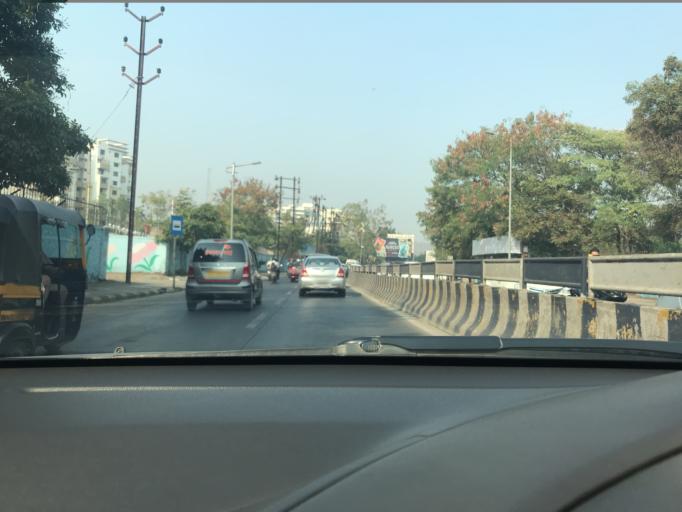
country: IN
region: Maharashtra
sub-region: Pune Division
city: Khadki
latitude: 18.5505
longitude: 73.8064
